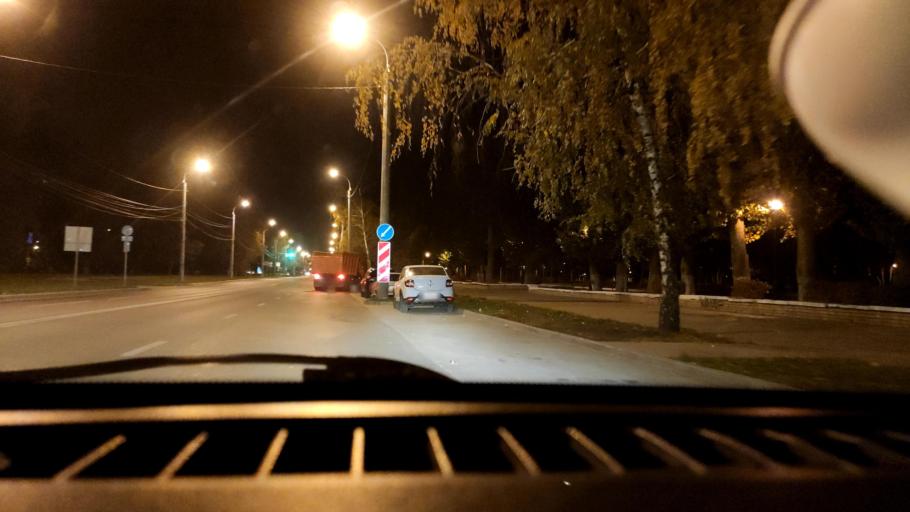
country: RU
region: Samara
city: Samara
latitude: 53.2280
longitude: 50.2051
